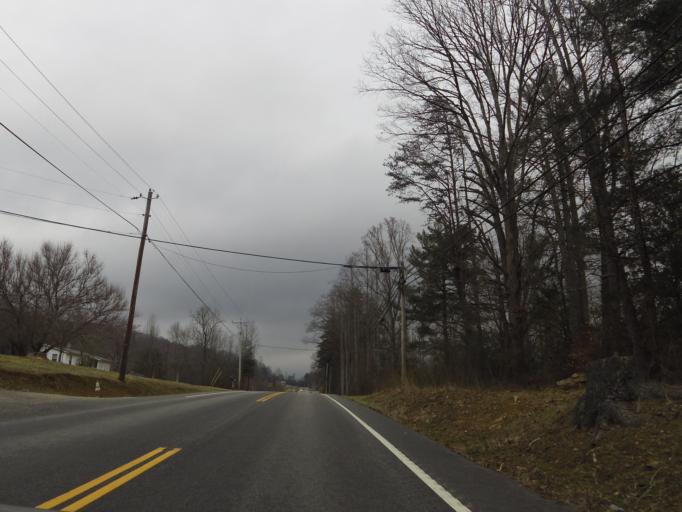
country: US
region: Tennessee
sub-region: Morgan County
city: Wartburg
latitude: 36.0619
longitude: -84.5354
